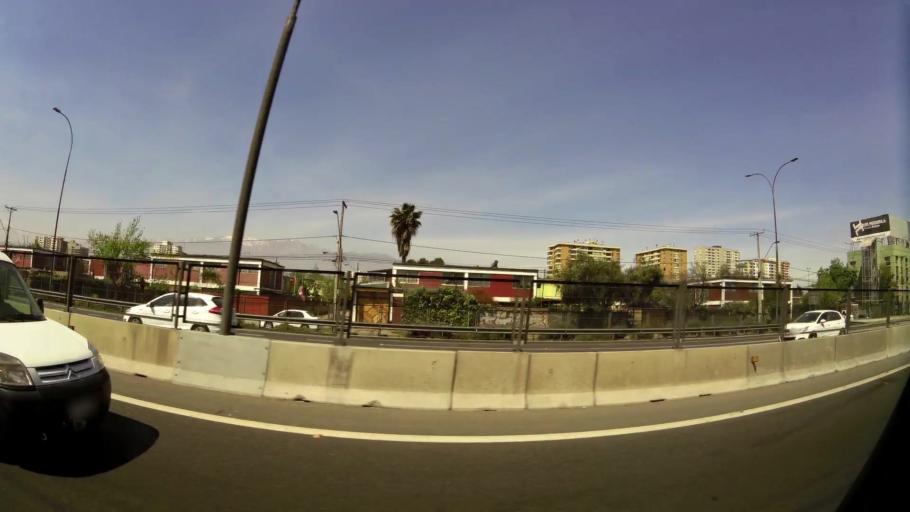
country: CL
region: Santiago Metropolitan
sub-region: Provincia de Santiago
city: Santiago
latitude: -33.4880
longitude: -70.6602
